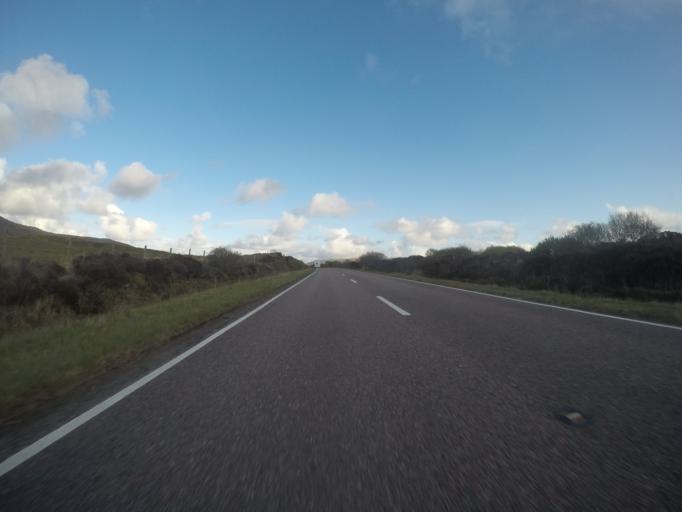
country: GB
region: Scotland
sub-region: Highland
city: Portree
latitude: 57.4624
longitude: -6.2821
